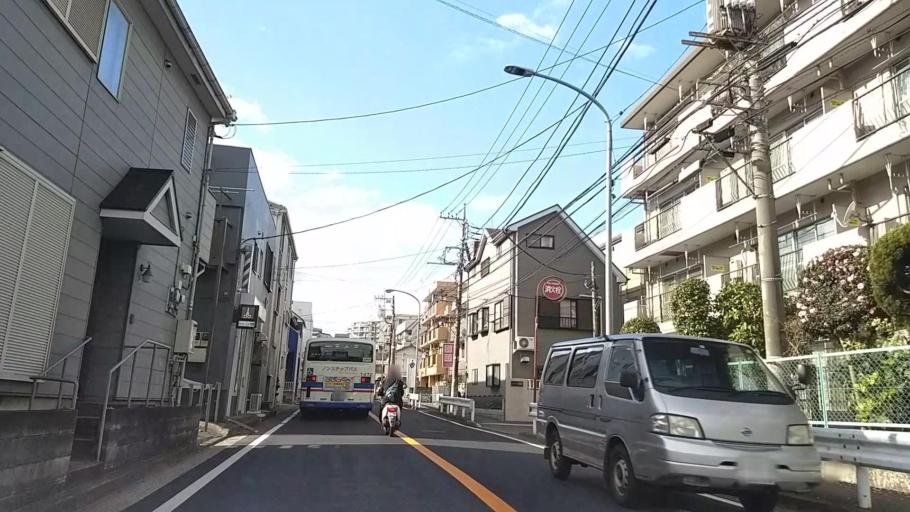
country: JP
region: Kanagawa
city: Yokohama
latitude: 35.5031
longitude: 139.6415
